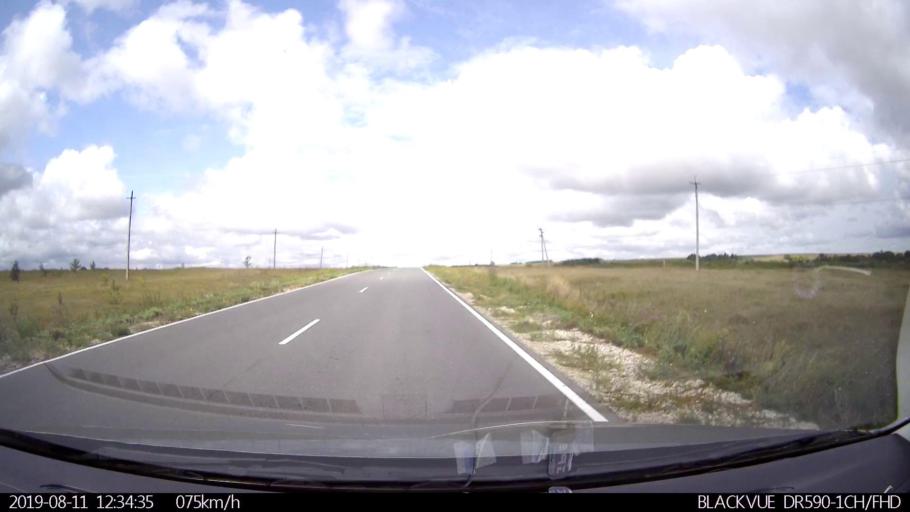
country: RU
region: Ulyanovsk
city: Ignatovka
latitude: 53.8180
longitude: 47.8408
